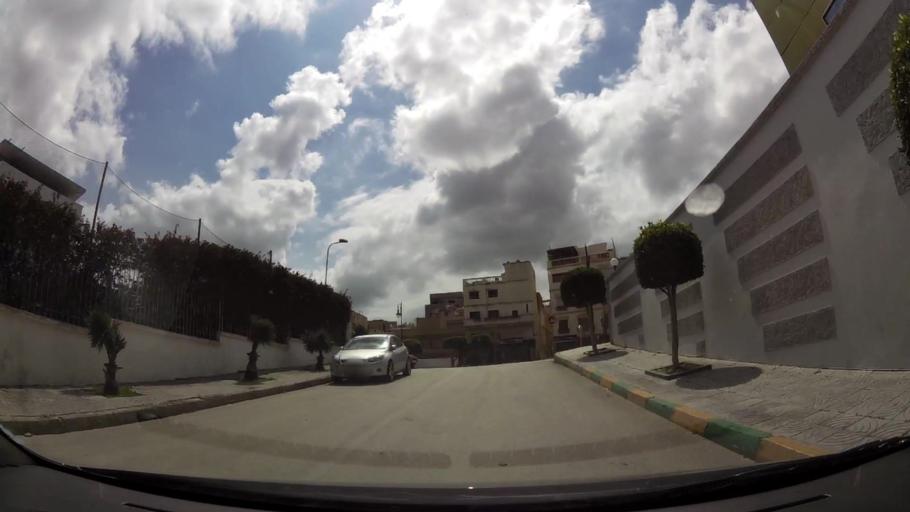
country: MA
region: Tanger-Tetouan
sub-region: Tanger-Assilah
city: Tangier
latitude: 35.7724
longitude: -5.7701
